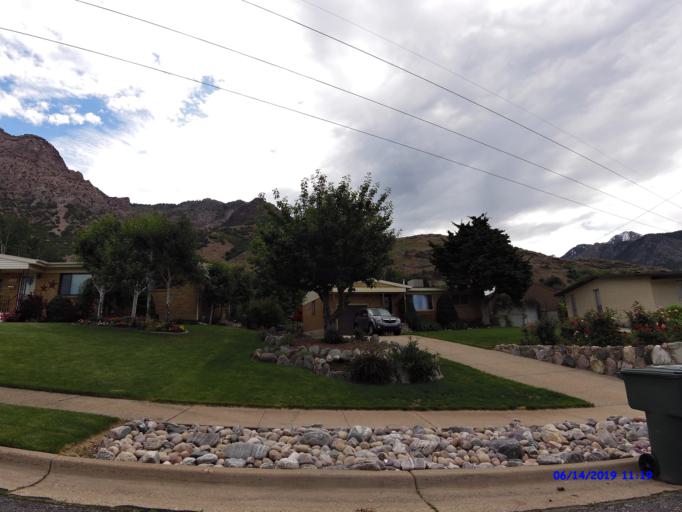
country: US
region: Utah
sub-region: Weber County
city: Ogden
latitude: 41.2532
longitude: -111.9390
